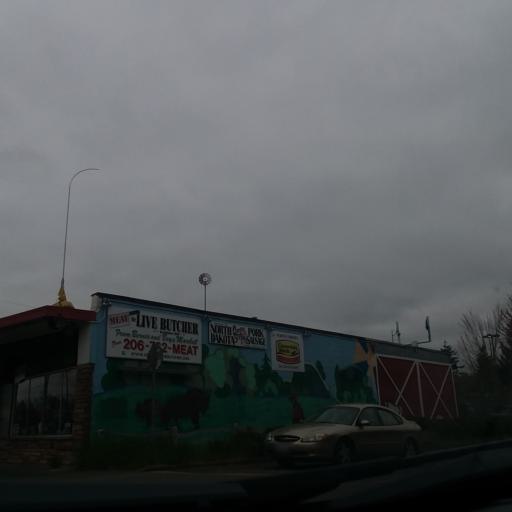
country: US
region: Washington
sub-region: King County
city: White Center
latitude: 47.5181
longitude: -122.3551
